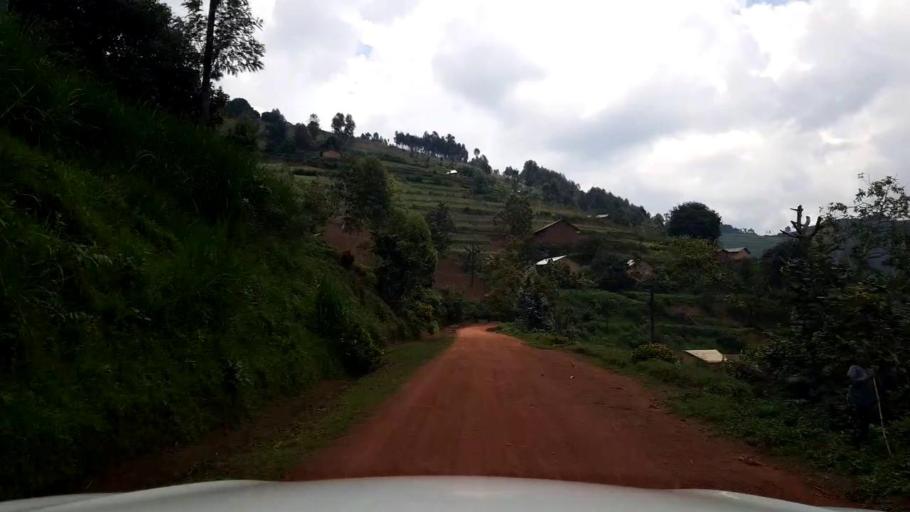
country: RW
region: Northern Province
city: Byumba
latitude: -1.4786
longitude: 29.9009
